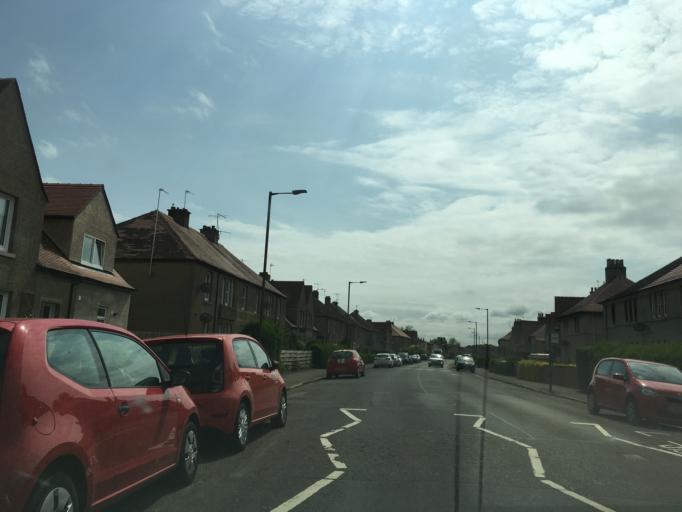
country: GB
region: Scotland
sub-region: Stirling
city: Stirling
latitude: 56.1114
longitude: -3.9307
